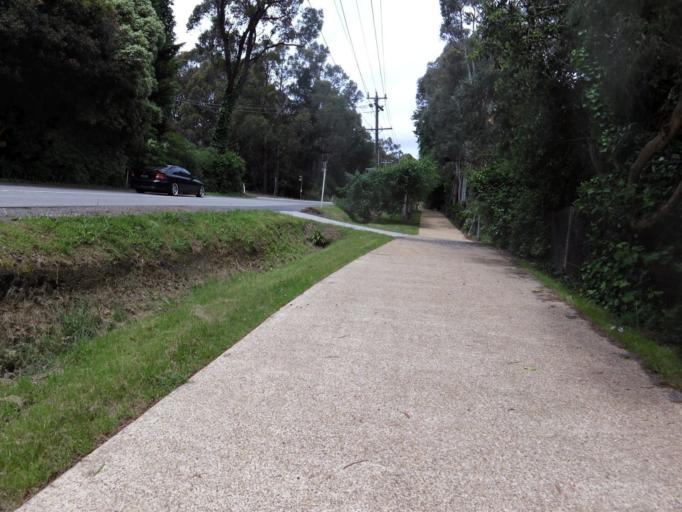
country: AU
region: Victoria
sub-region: Cardinia
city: Cockatoo
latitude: -37.9383
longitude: 145.4956
